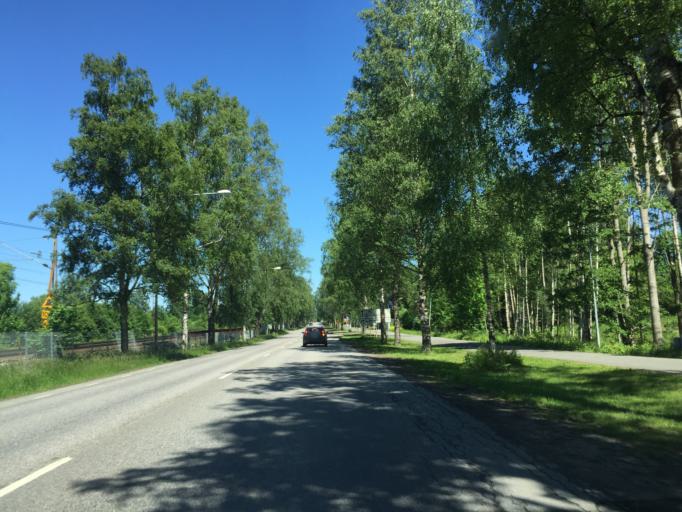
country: SE
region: OErebro
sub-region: Orebro Kommun
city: Orebro
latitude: 59.2562
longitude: 15.1862
